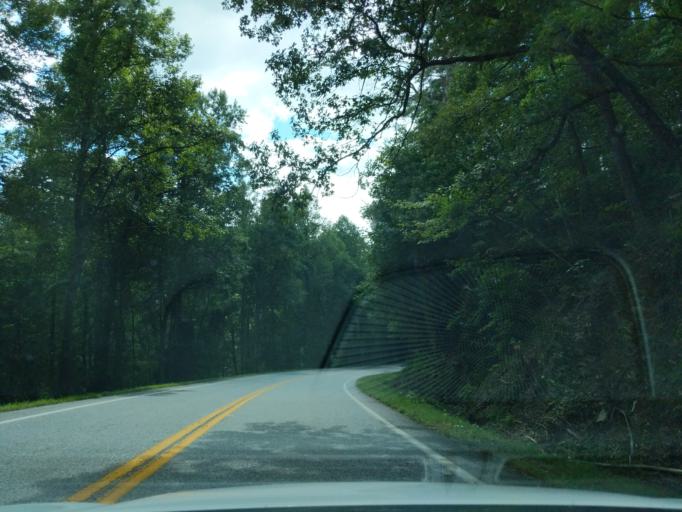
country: US
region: Georgia
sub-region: White County
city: Cleveland
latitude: 34.6788
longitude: -83.8958
